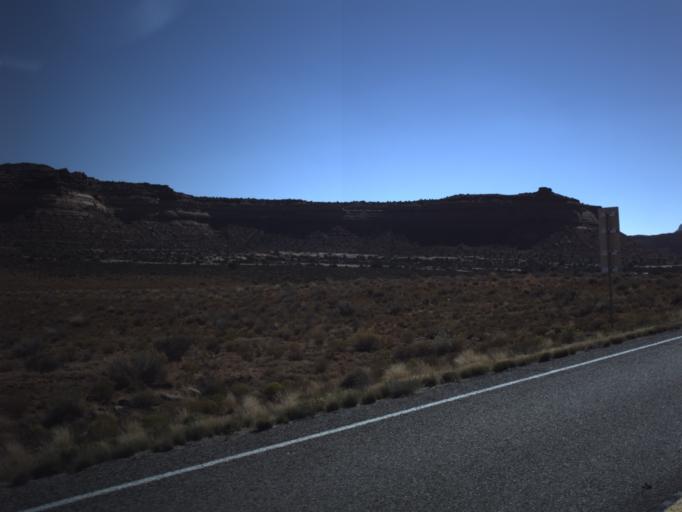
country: US
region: Utah
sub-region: San Juan County
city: Blanding
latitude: 37.7578
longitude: -110.2823
